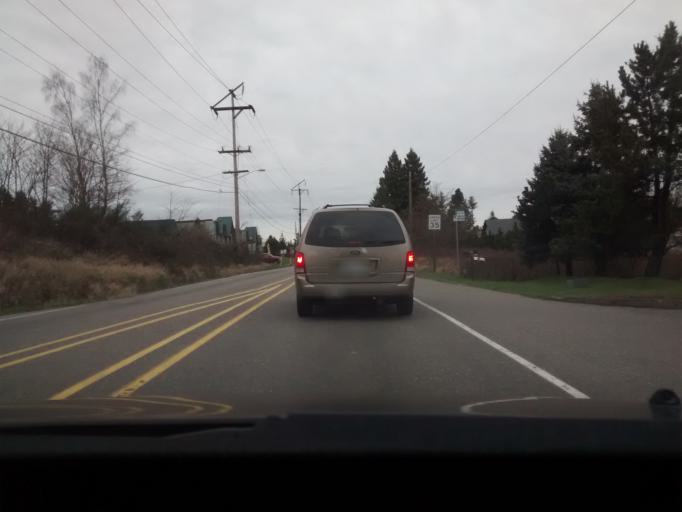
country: US
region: Washington
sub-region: Kitsap County
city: Bethel
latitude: 47.5059
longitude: -122.6314
